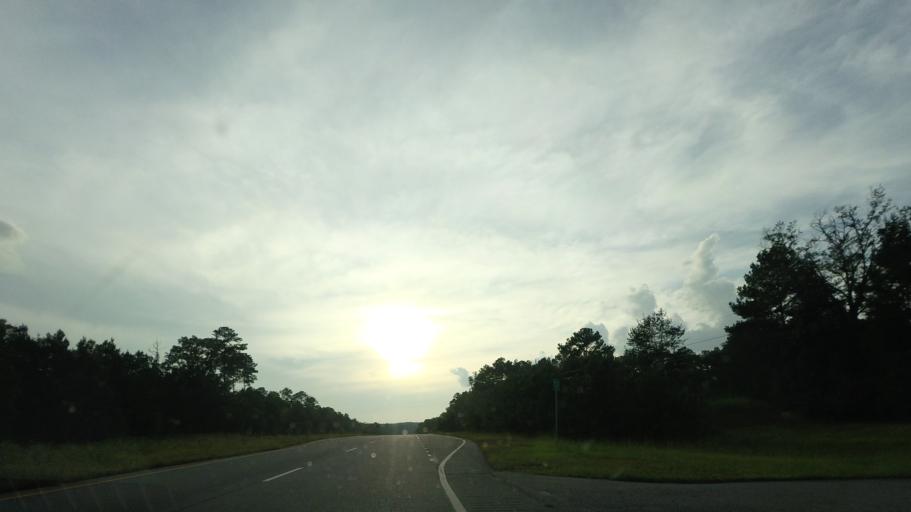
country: US
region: Georgia
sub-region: Wilkinson County
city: Gordon
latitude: 32.8482
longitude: -83.4434
